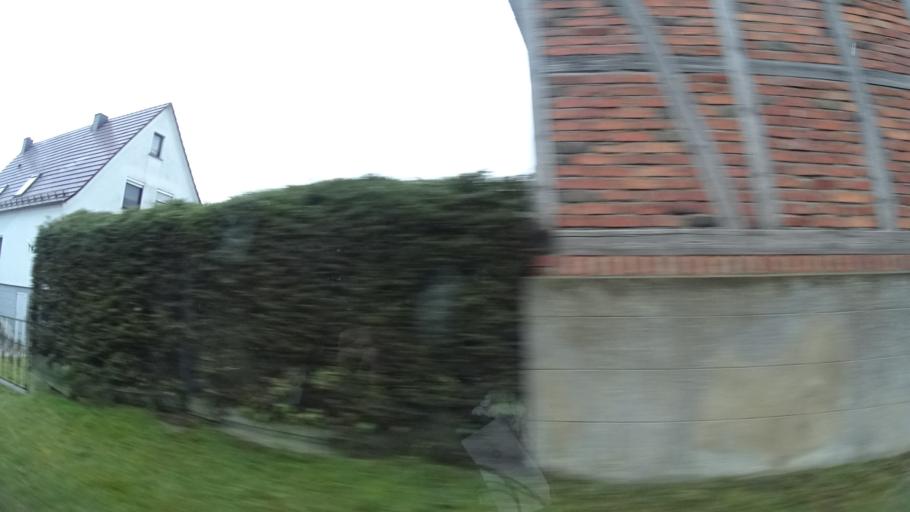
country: DE
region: Thuringia
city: Kaltenwestheim
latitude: 50.6093
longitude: 10.1209
